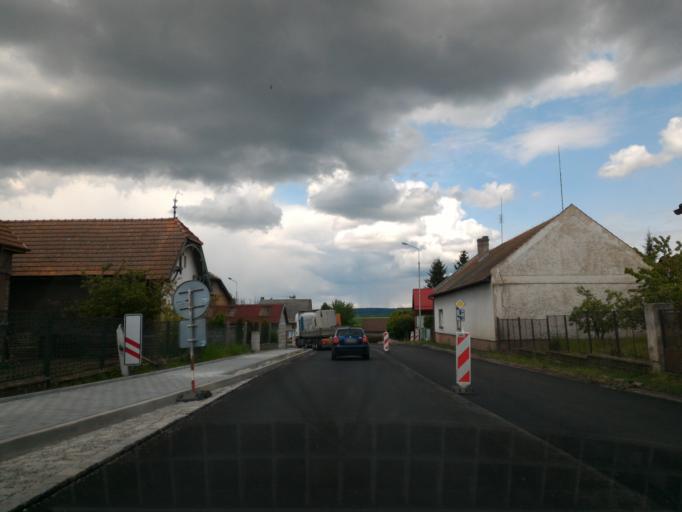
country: CZ
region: Central Bohemia
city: Lustenice
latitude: 50.3084
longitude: 14.9533
